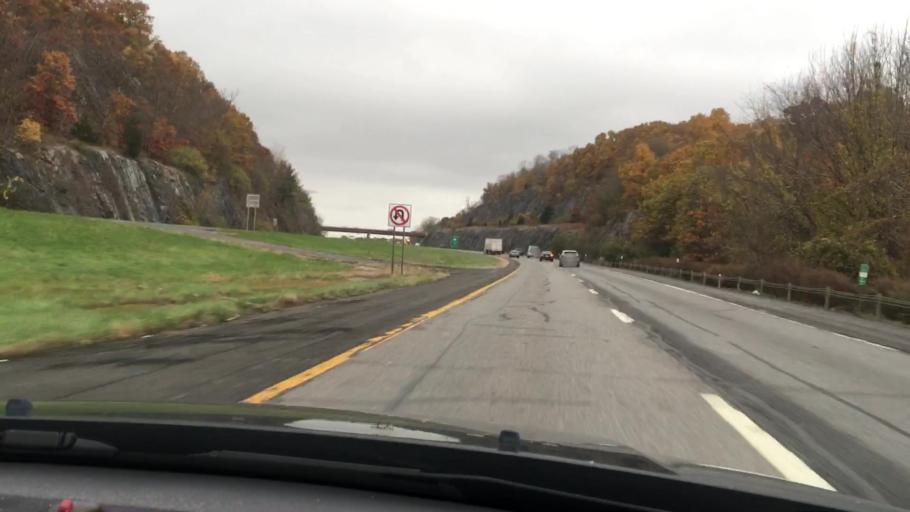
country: US
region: New York
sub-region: Putnam County
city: Brewster Hill
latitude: 41.4208
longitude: -73.6229
